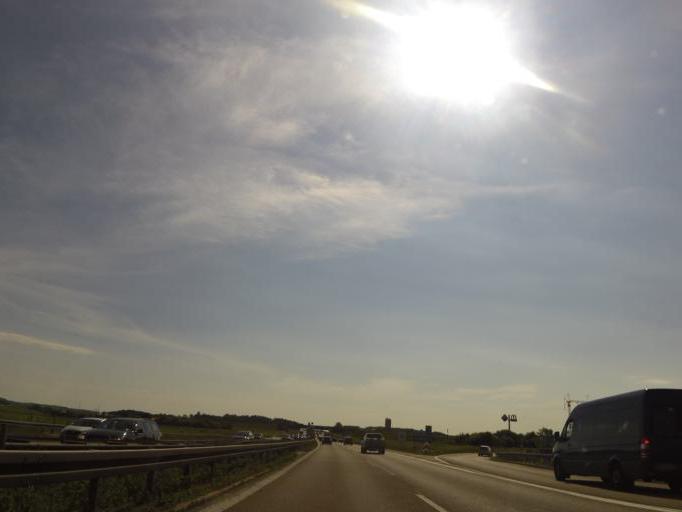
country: DE
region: Baden-Wuerttemberg
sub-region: Tuebingen Region
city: Merklingen
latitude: 48.5184
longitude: 9.7554
